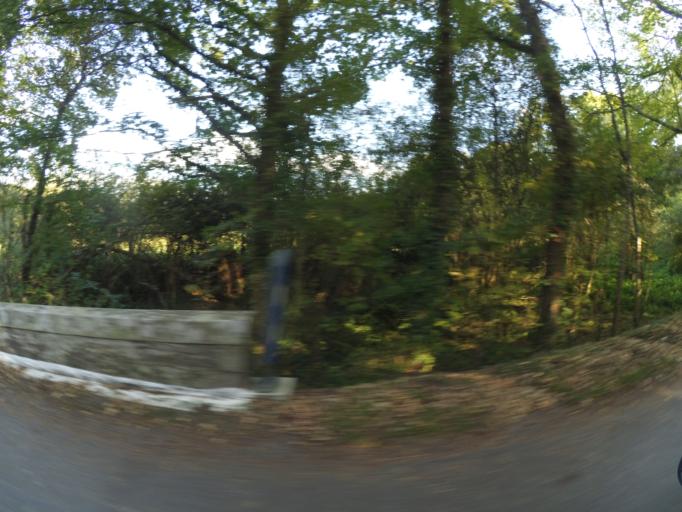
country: FR
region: Brittany
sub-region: Departement du Morbihan
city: Saint-Vincent-sur-Oust
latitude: 47.7196
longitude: -2.1698
